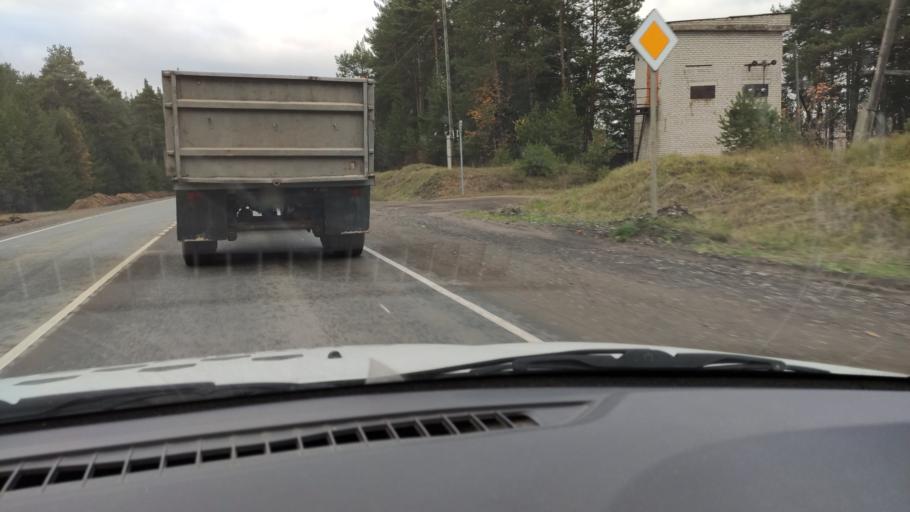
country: RU
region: Kirov
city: Belaya Kholunitsa
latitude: 58.8506
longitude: 50.8290
